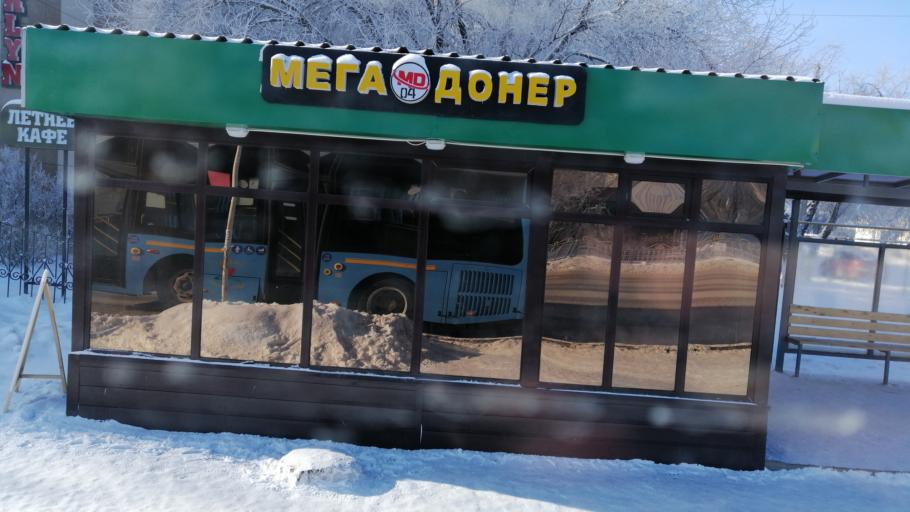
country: KZ
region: Aqtoebe
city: Aqtobe
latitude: 50.3066
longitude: 57.1498
